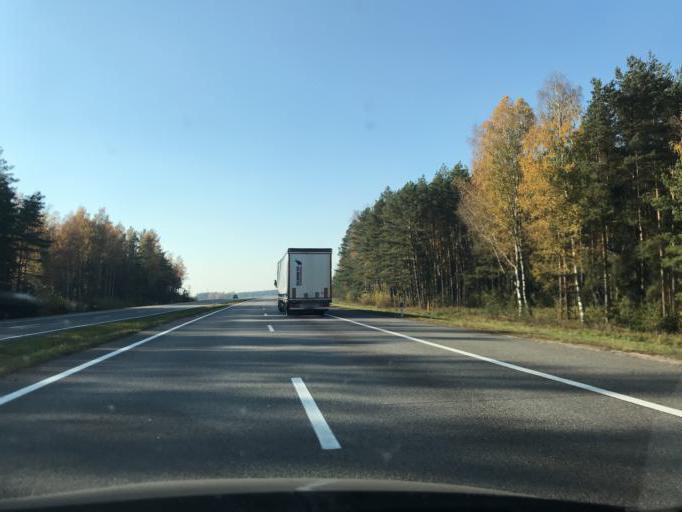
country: BY
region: Minsk
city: Stowbtsy
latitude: 53.5293
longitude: 26.8530
